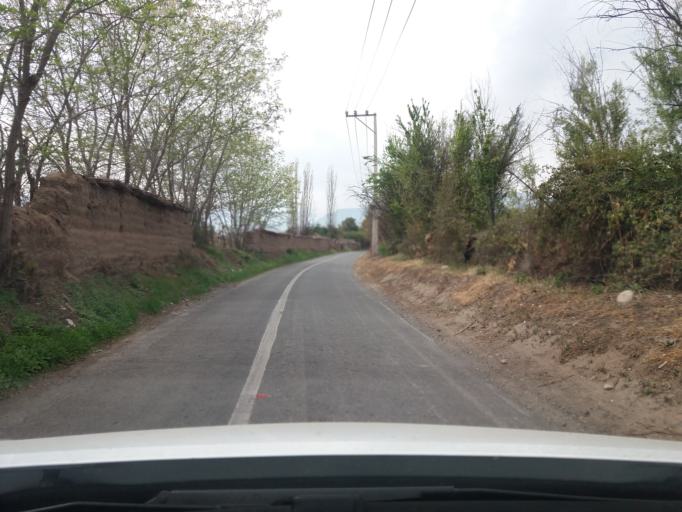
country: CL
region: Valparaiso
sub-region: Provincia de Los Andes
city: Los Andes
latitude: -32.8285
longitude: -70.6346
